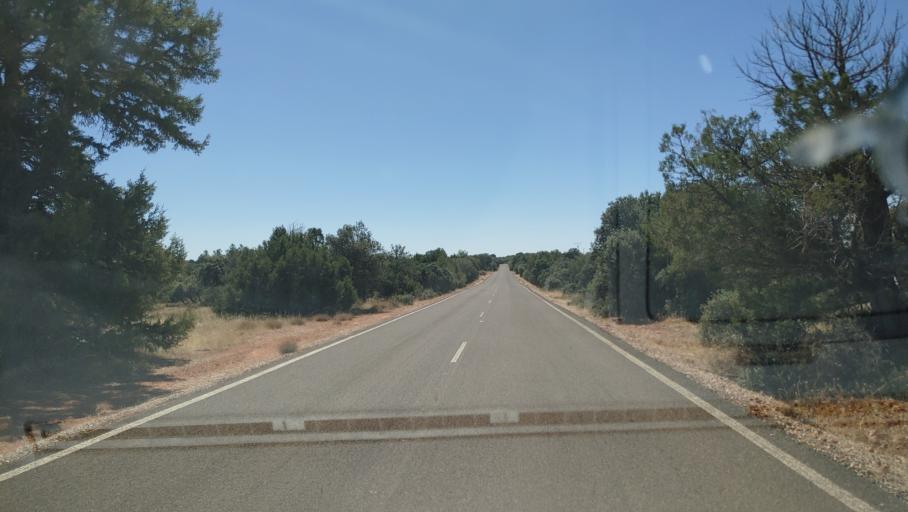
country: ES
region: Castille-La Mancha
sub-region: Provincia de Ciudad Real
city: Villahermosa
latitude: 38.8401
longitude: -2.8145
